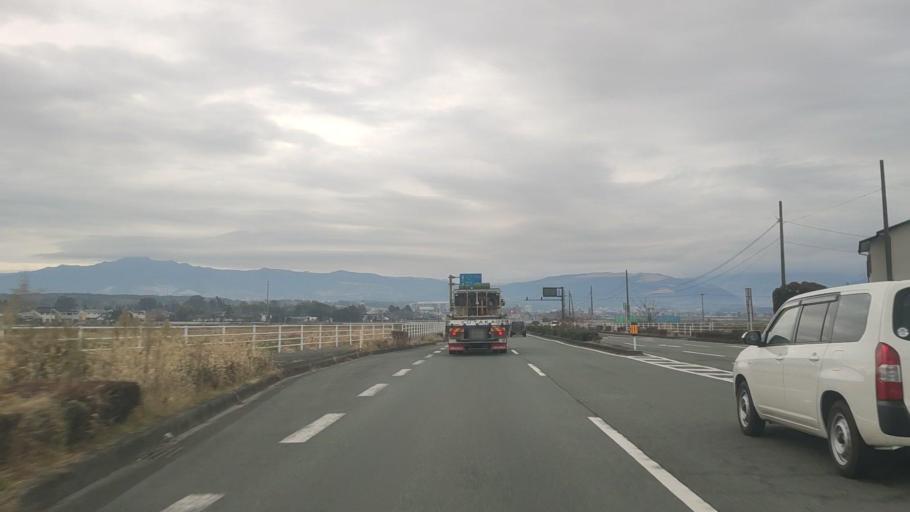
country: JP
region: Kumamoto
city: Ozu
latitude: 32.8660
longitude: 130.8317
